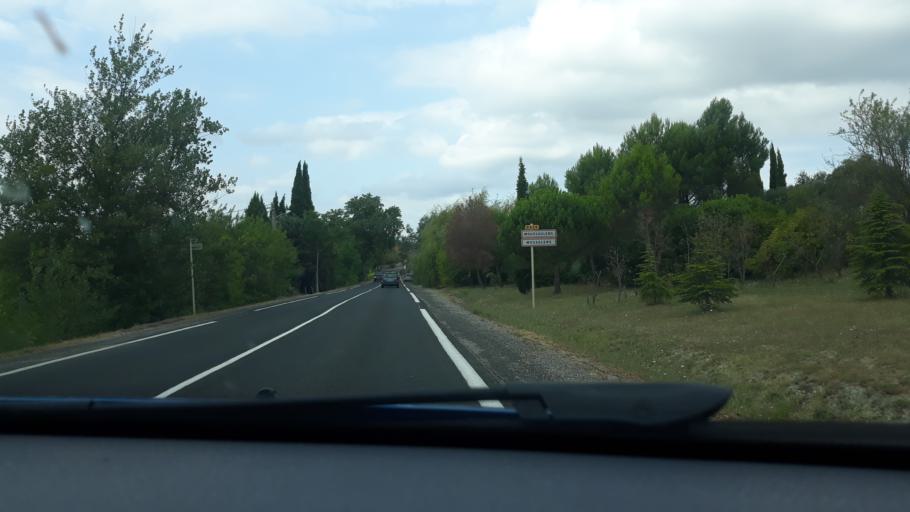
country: FR
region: Languedoc-Roussillon
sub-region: Departement de l'Aude
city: Pezens
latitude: 43.2760
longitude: 2.2325
